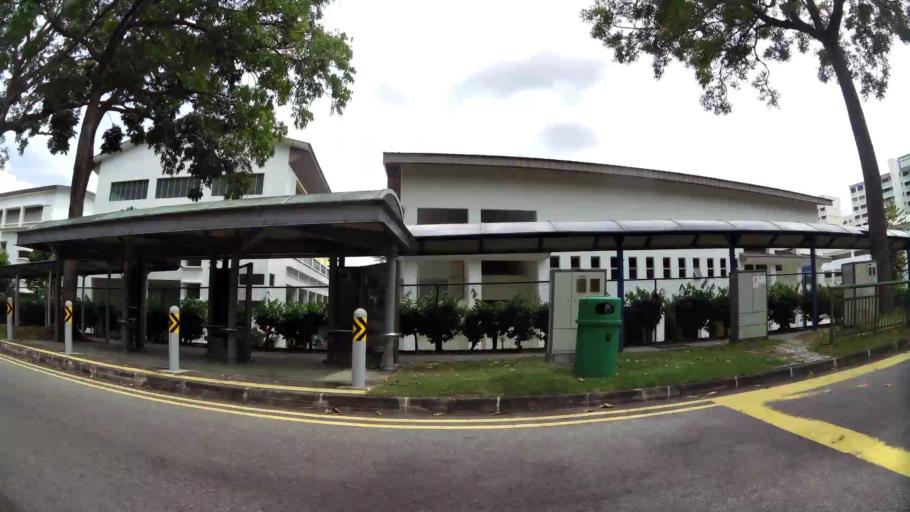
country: MY
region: Johor
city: Johor Bahru
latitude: 1.3826
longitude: 103.7730
